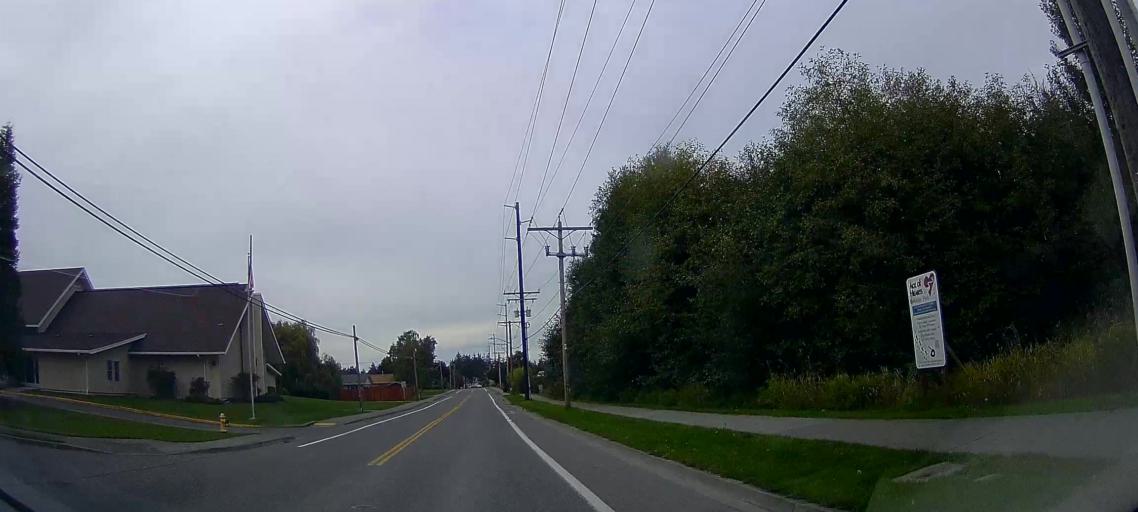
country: US
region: Washington
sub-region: Skagit County
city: Anacortes
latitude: 48.4908
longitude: -122.6252
